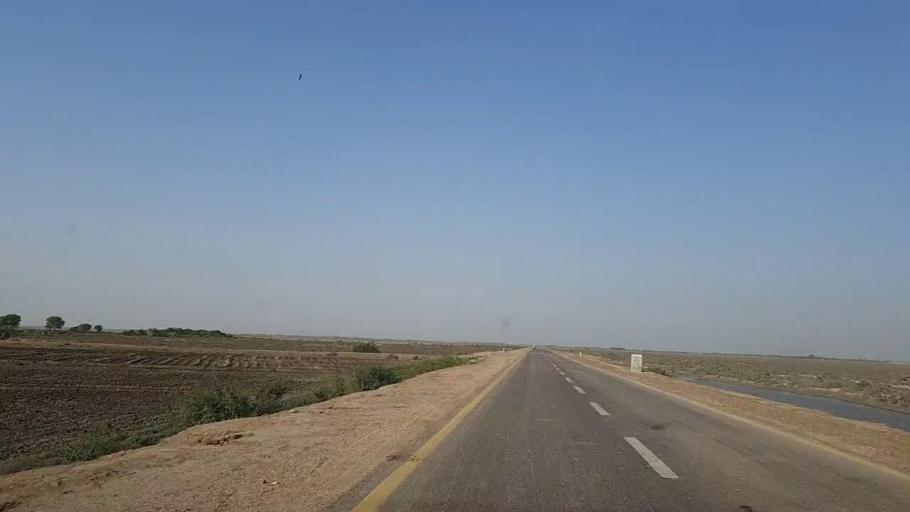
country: PK
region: Sindh
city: Jati
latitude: 24.4854
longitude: 68.3742
